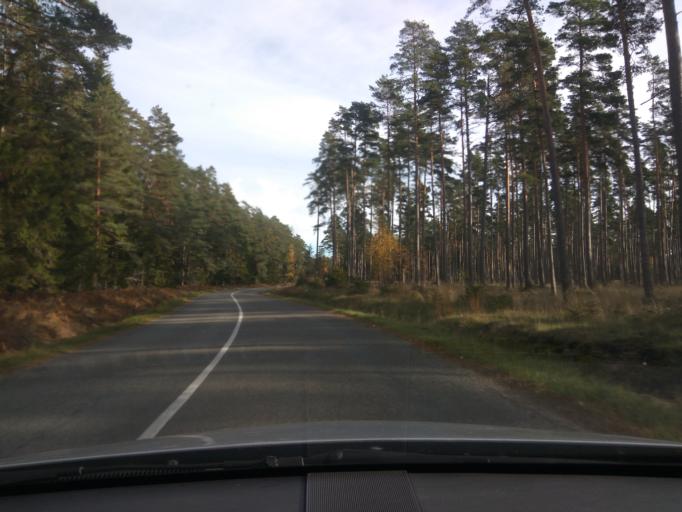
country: LV
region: Alsunga
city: Alsunga
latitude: 57.0128
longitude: 21.4262
